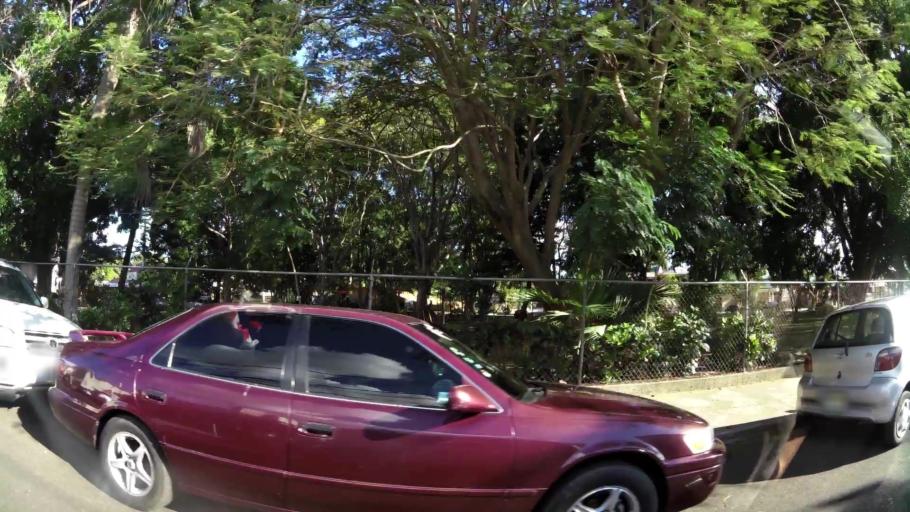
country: DO
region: Santiago
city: Santiago de los Caballeros
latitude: 19.4643
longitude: -70.6912
